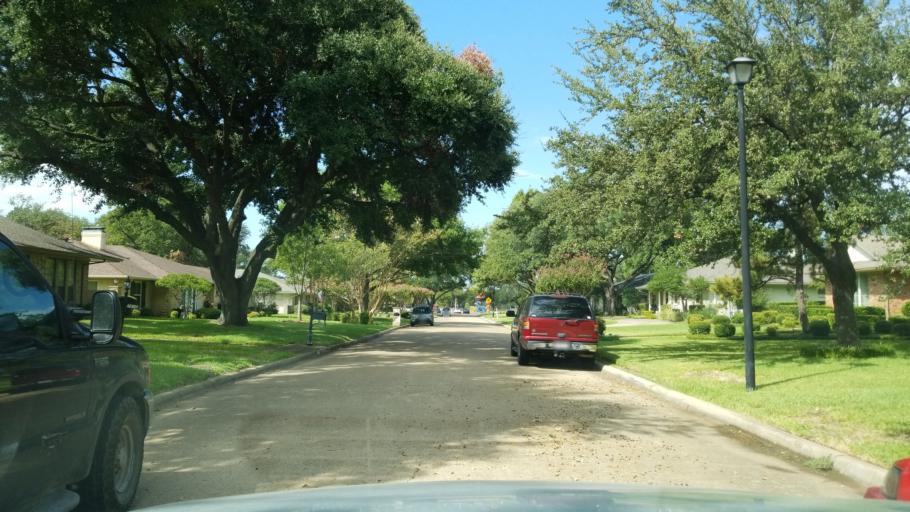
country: US
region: Texas
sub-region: Dallas County
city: Richardson
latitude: 32.9568
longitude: -96.7735
